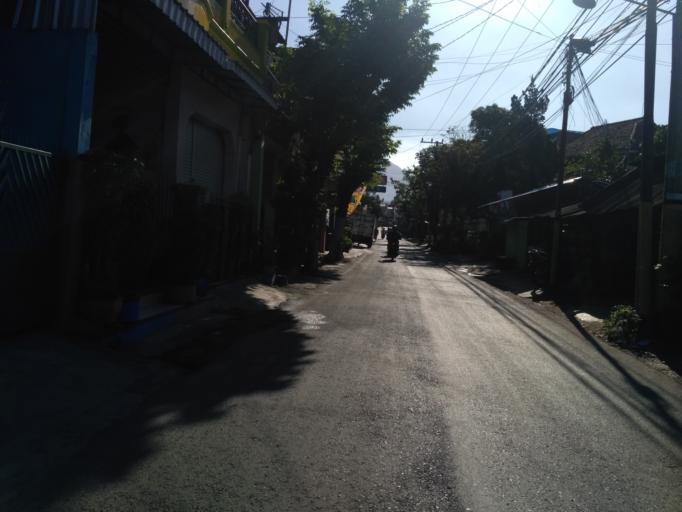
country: ID
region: East Java
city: Malang
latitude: -7.9446
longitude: 112.6065
